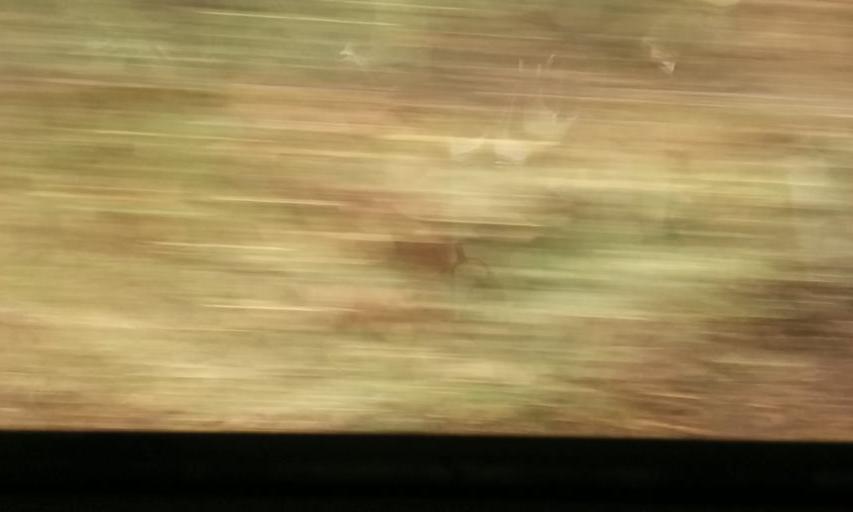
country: JP
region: Nagano
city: Iida
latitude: 35.6777
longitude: 137.6419
